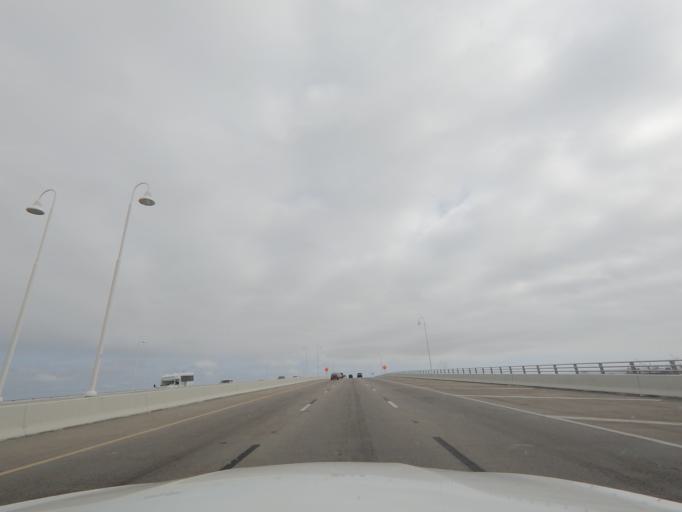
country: US
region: Florida
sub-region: Bay County
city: Upper Grand Lagoon
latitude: 30.1877
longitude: -85.7440
